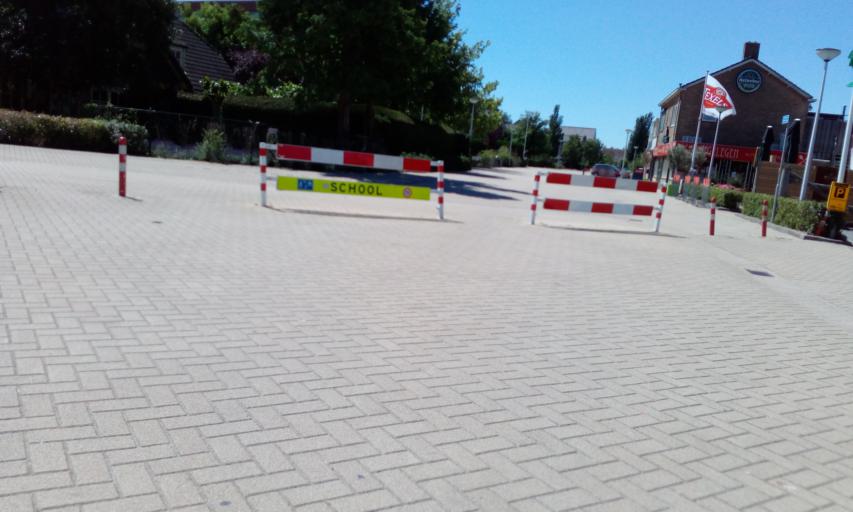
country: NL
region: South Holland
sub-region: Gemeente Teylingen
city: Voorhout
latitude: 52.2285
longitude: 4.4910
